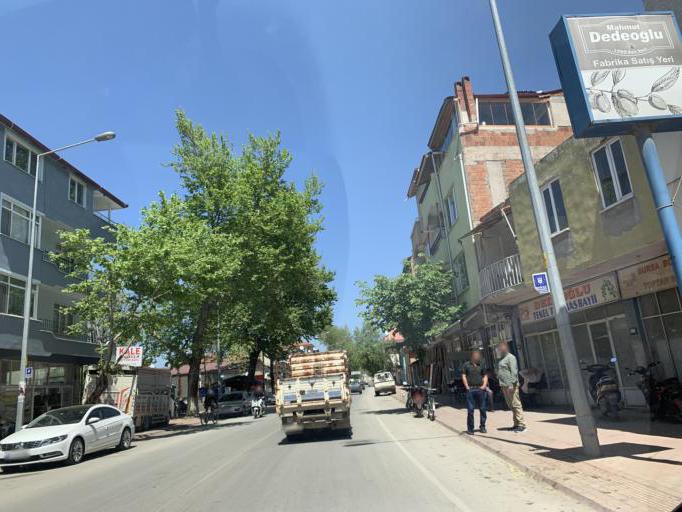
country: TR
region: Bursa
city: Iznik
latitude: 40.4246
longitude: 29.7194
